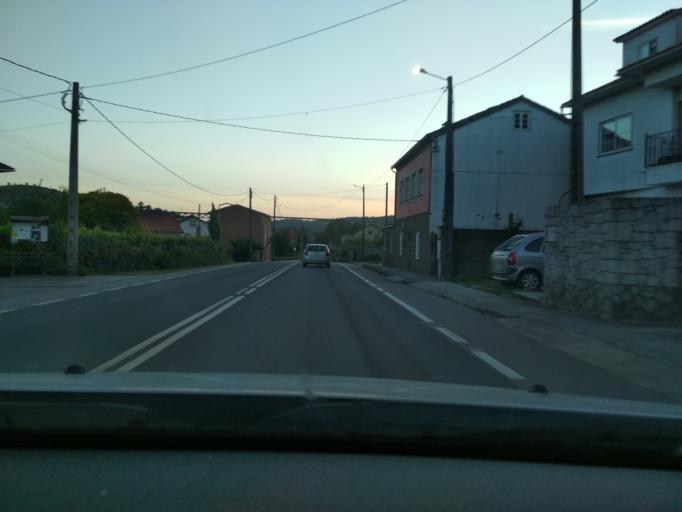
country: ES
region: Galicia
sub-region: Provincia de Pontevedra
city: Catoira
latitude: 42.6688
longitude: -8.7166
